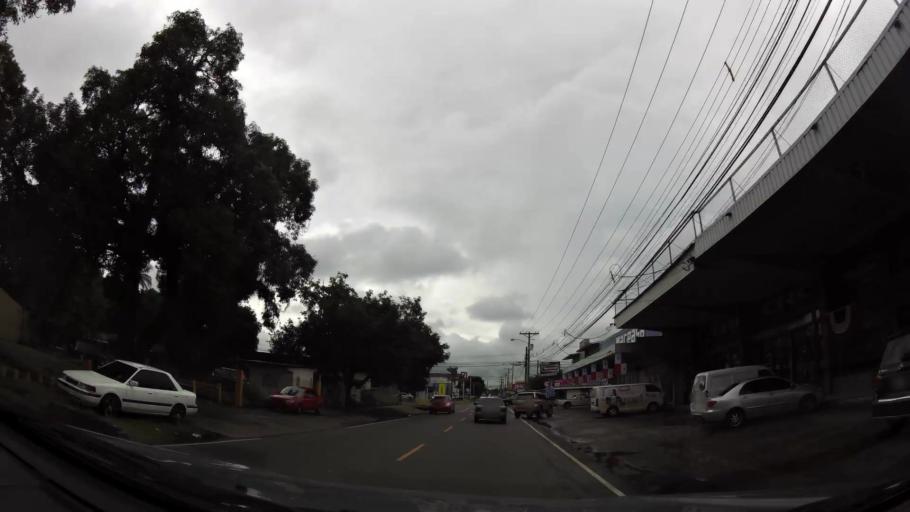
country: PA
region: Chiriqui
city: David
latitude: 8.4253
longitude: -82.4340
